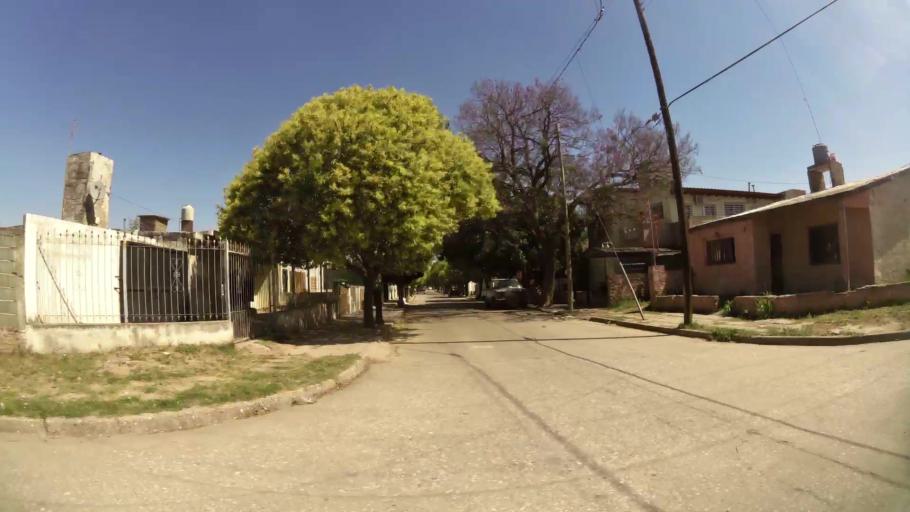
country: AR
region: Cordoba
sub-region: Departamento de Capital
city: Cordoba
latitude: -31.3657
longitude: -64.1401
